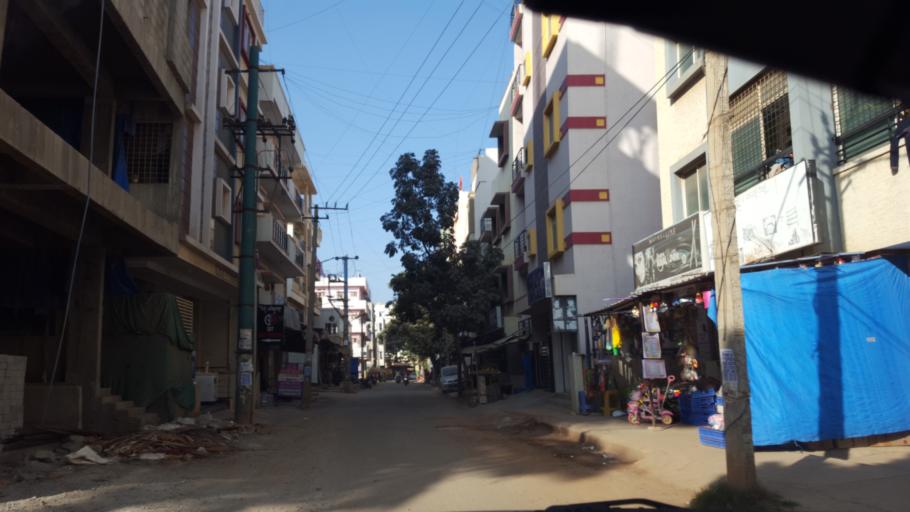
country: IN
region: Karnataka
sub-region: Bangalore Urban
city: Bangalore
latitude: 12.9495
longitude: 77.7092
